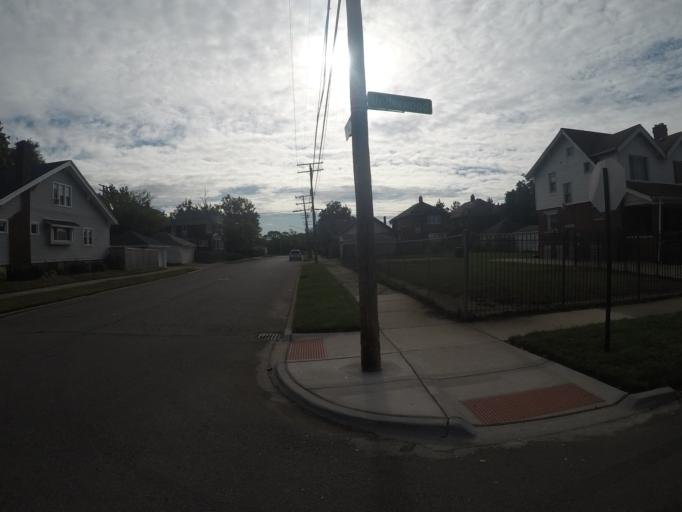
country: US
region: Michigan
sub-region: Wayne County
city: Highland Park
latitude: 42.3627
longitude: -83.1352
